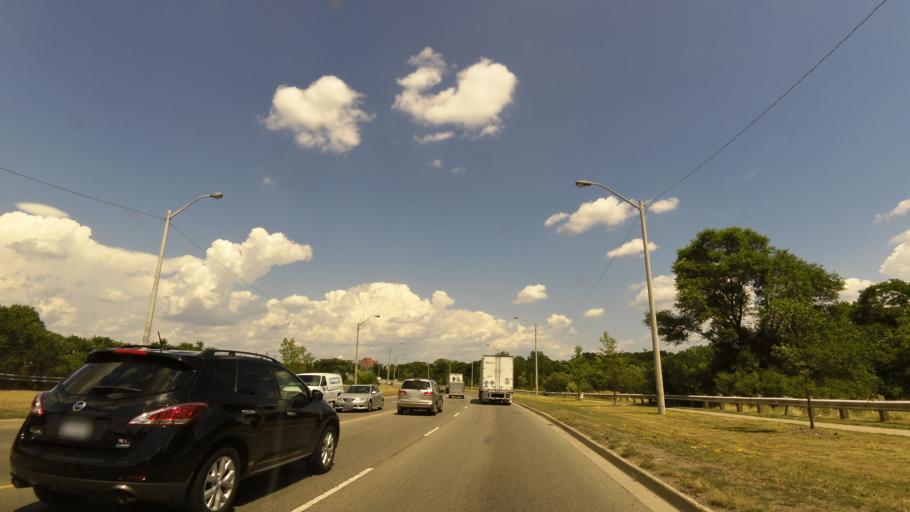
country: CA
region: Ontario
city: Etobicoke
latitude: 43.7603
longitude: -79.5836
